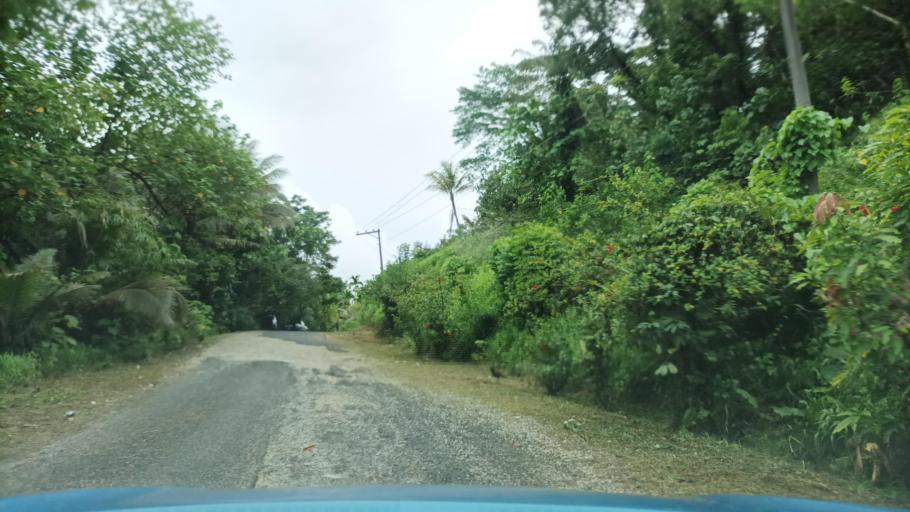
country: FM
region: Pohnpei
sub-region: Sokehs Municipality
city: Palikir - National Government Center
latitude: 6.8238
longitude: 158.1673
